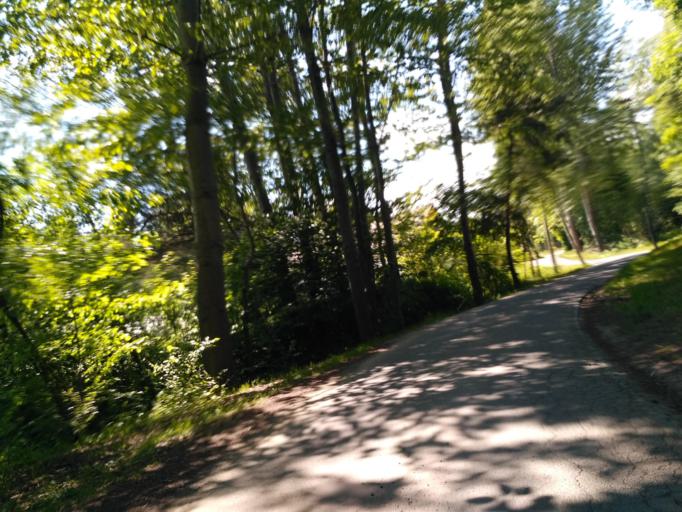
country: PL
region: Subcarpathian Voivodeship
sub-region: Powiat krosnienski
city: Miejsce Piastowe
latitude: 49.6554
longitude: 21.7615
